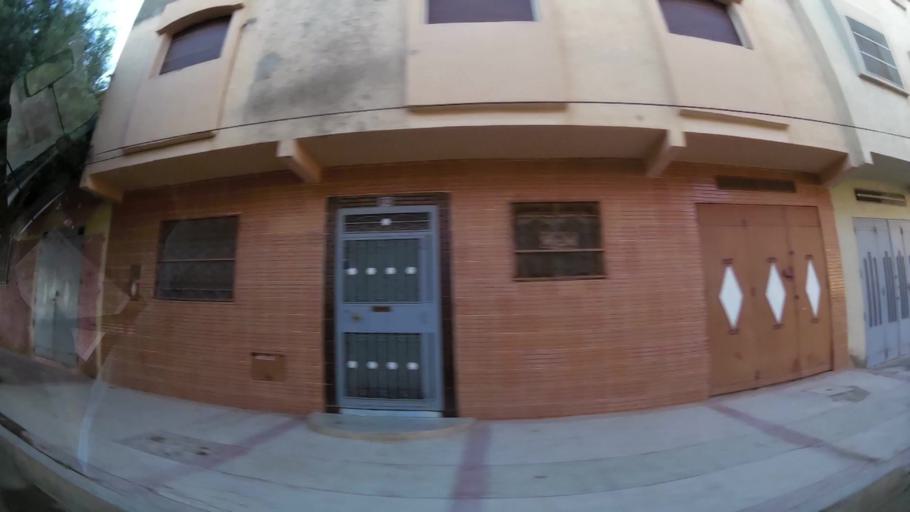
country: MA
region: Oriental
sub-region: Oujda-Angad
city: Oujda
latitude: 34.7069
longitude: -1.9217
